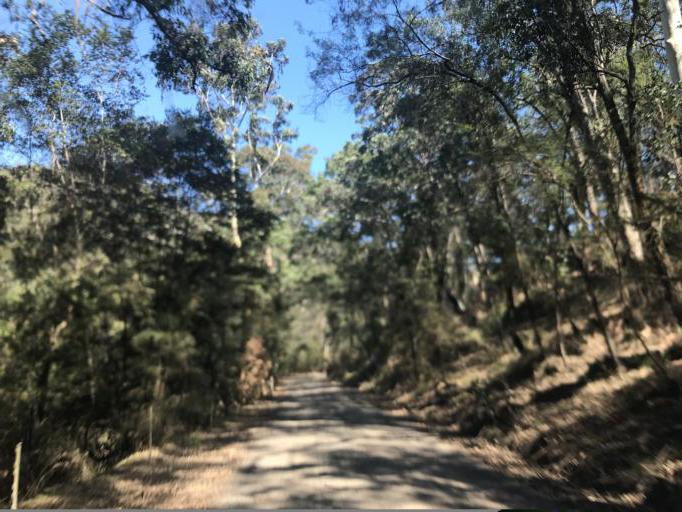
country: AU
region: New South Wales
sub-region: Wyong Shire
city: Little Jilliby
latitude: -33.1966
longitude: 151.0190
